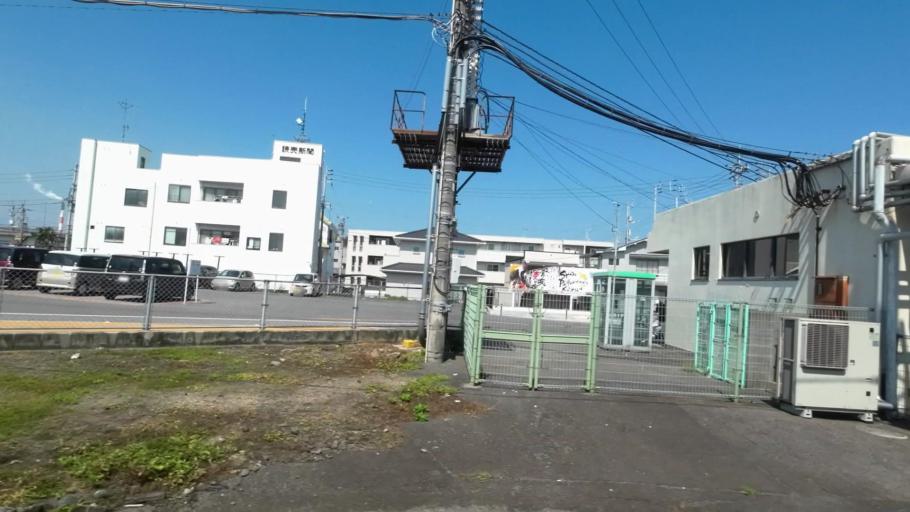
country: JP
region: Ehime
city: Kawanoecho
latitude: 34.0141
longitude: 133.5759
